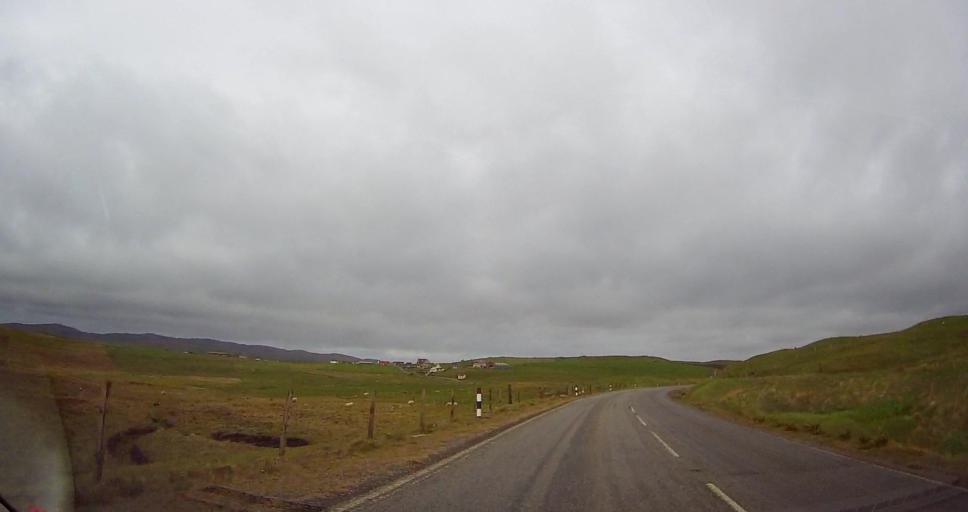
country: GB
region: Scotland
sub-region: Shetland Islands
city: Lerwick
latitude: 60.3711
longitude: -1.3319
